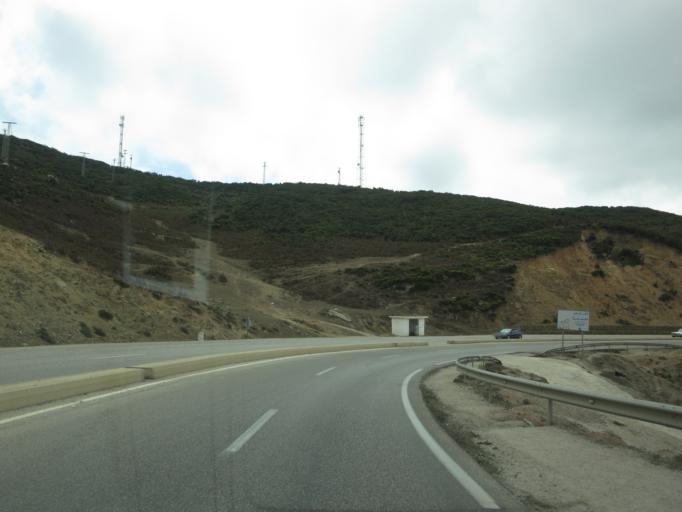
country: ES
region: Ceuta
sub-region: Ceuta
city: Ceuta
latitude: 35.8545
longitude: -5.4332
